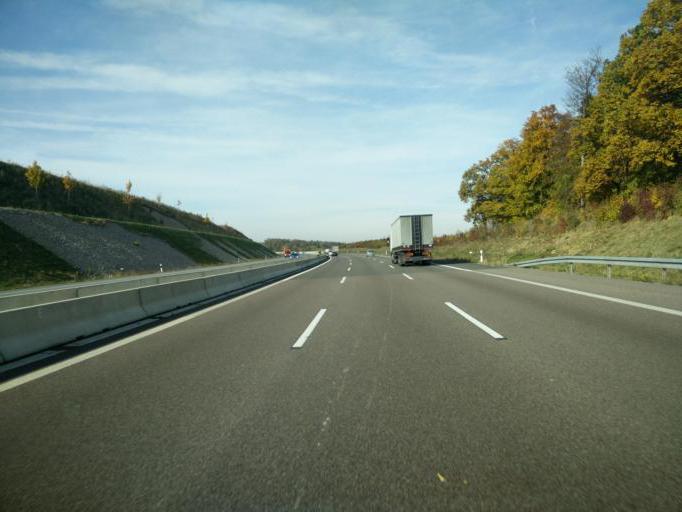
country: DE
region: Baden-Wuerttemberg
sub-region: Karlsruhe Region
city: Friolzheim
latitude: 48.8391
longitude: 8.8454
